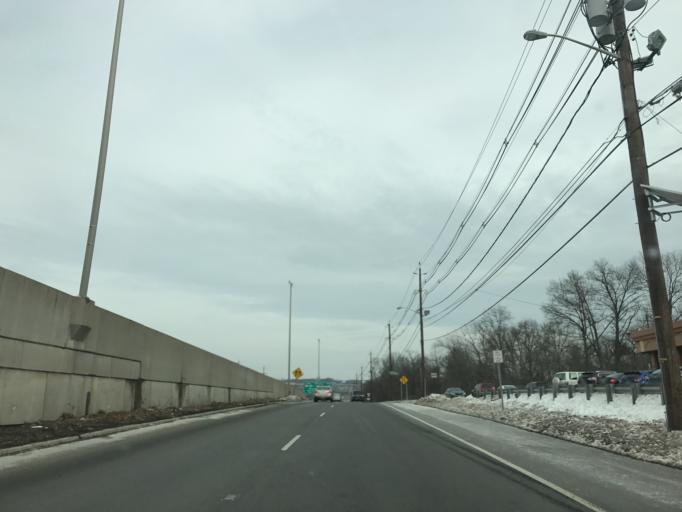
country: US
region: New Jersey
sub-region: Somerset County
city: Raritan
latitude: 40.5768
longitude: -74.6272
